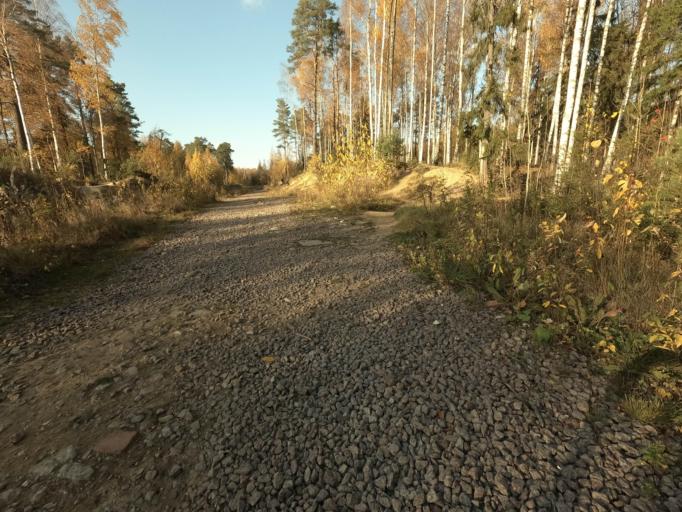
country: RU
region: Leningrad
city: Sertolovo
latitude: 60.1501
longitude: 30.2224
